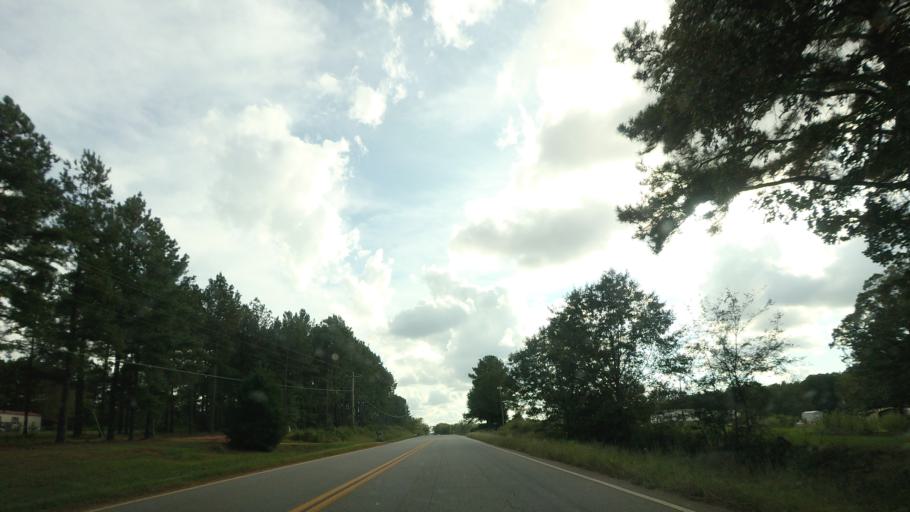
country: US
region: Georgia
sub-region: Pulaski County
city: Hawkinsville
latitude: 32.3045
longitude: -83.4258
